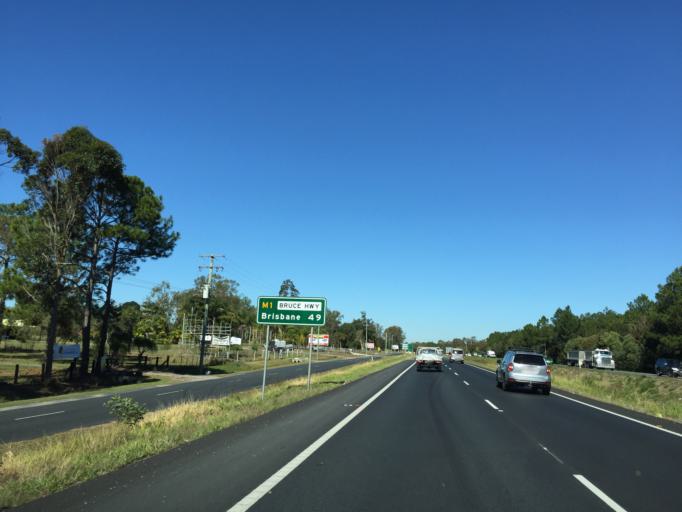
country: AU
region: Queensland
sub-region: Moreton Bay
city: Caboolture
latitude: -27.0486
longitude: 152.9774
